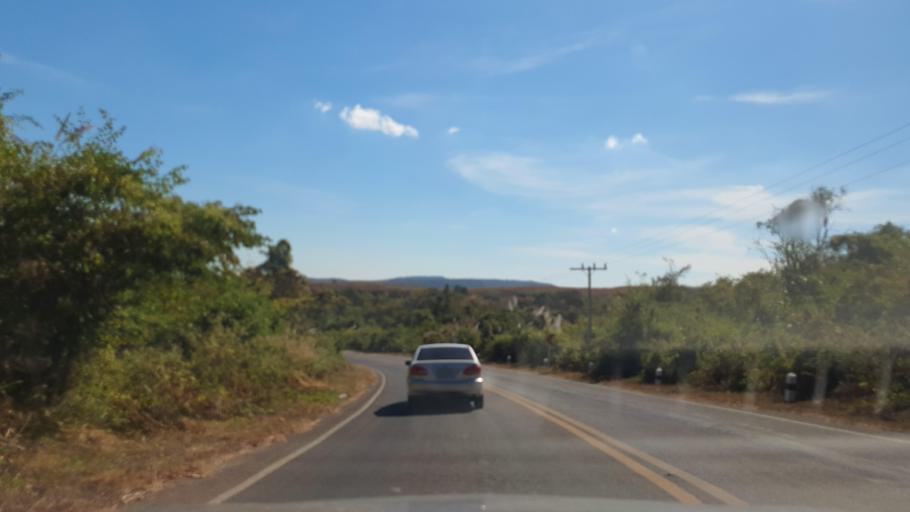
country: TH
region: Kalasin
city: Khao Wong
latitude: 16.7953
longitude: 104.1371
